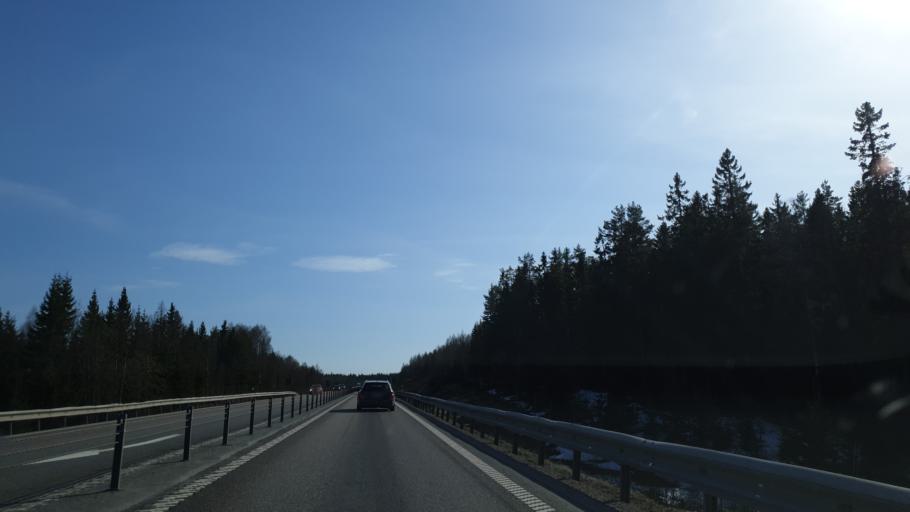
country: SE
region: Vaesternorrland
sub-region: Sundsvalls Kommun
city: Njurundabommen
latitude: 62.2025
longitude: 17.3719
